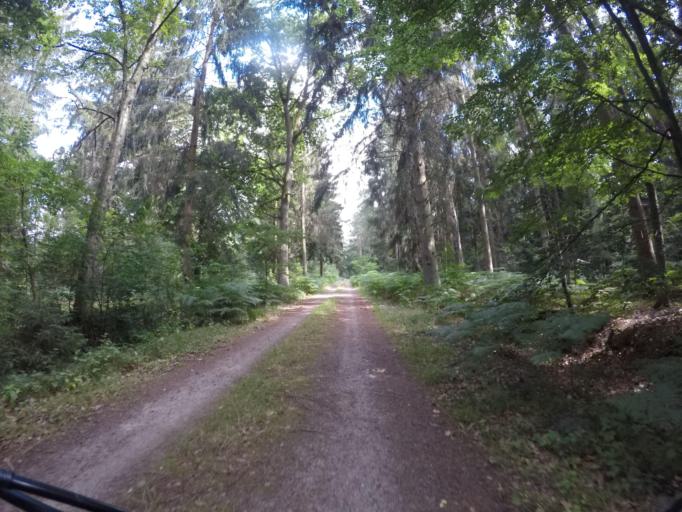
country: DE
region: Lower Saxony
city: Neu Darchau
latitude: 53.2856
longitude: 10.9685
